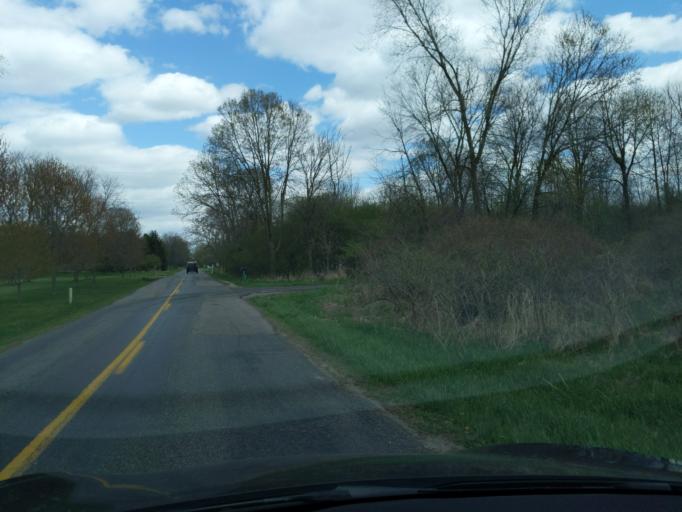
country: US
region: Michigan
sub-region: Eaton County
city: Dimondale
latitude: 42.6257
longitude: -84.5914
